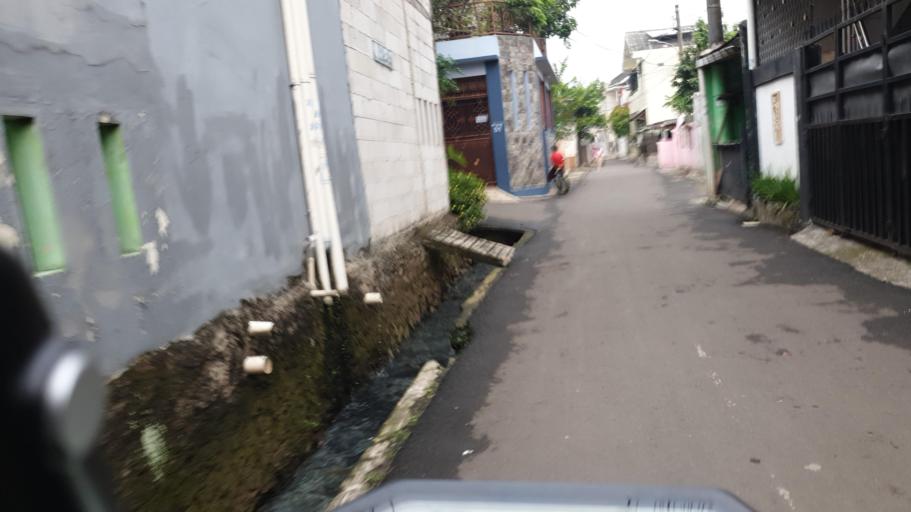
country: ID
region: West Java
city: Depok
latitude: -6.3435
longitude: 106.8242
